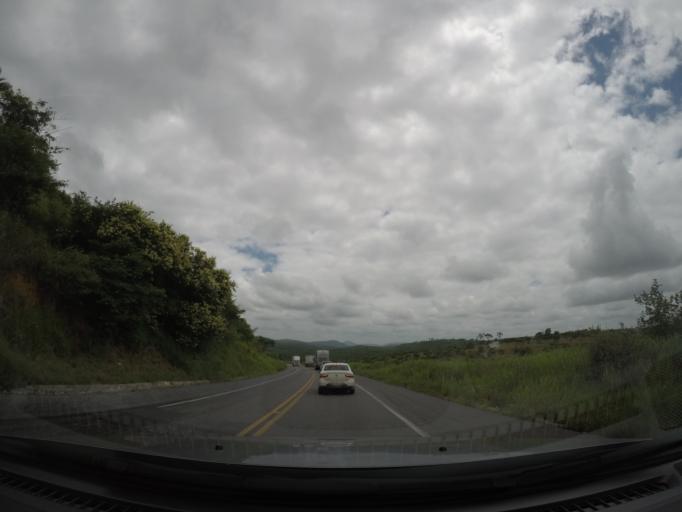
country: BR
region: Bahia
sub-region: Ruy Barbosa
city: Terra Nova
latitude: -12.4574
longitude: -40.5877
